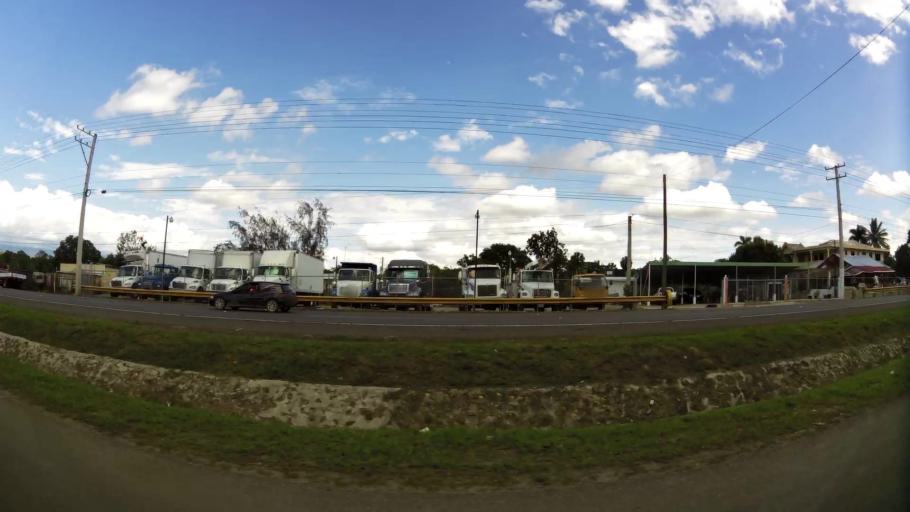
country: DO
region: La Vega
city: Rio Verde Arriba
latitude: 19.3591
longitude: -70.6018
